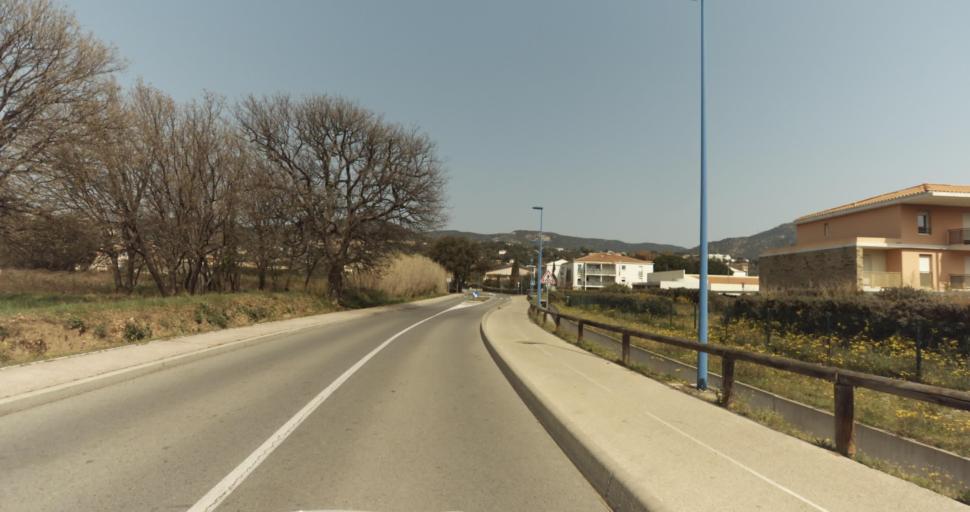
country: FR
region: Provence-Alpes-Cote d'Azur
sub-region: Departement du Var
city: Bormes-les-Mimosas
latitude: 43.1374
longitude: 6.3462
